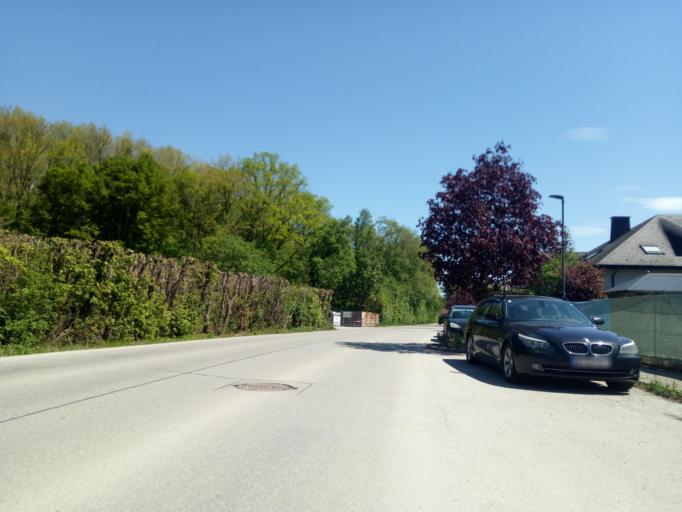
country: AT
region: Lower Austria
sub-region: Politischer Bezirk Modling
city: Kaltenleutgeben
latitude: 48.1302
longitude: 16.1889
